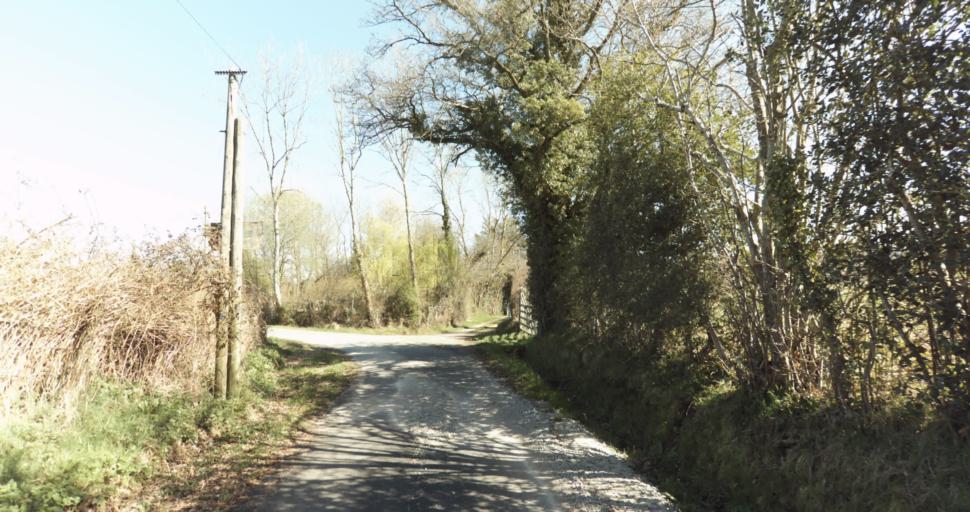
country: FR
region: Lower Normandy
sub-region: Departement du Calvados
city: Livarot
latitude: 48.9855
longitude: 0.0715
